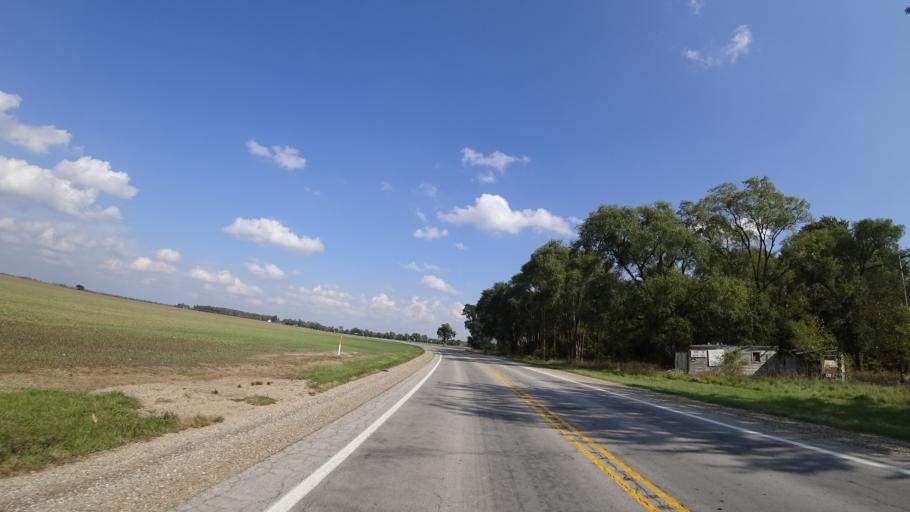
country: US
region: Michigan
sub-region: Saint Joseph County
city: Colon
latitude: 42.0106
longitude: -85.3667
